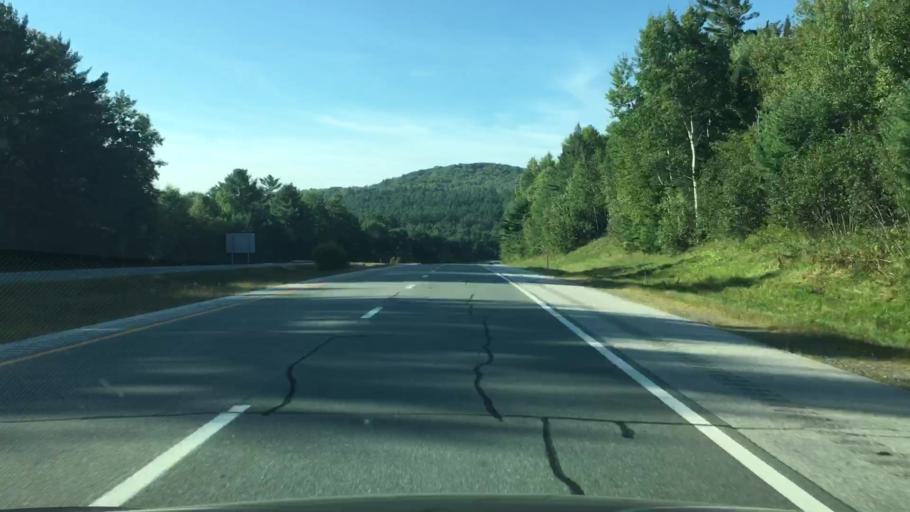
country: US
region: New Hampshire
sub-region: Grafton County
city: Littleton
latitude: 44.2427
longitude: -71.7588
